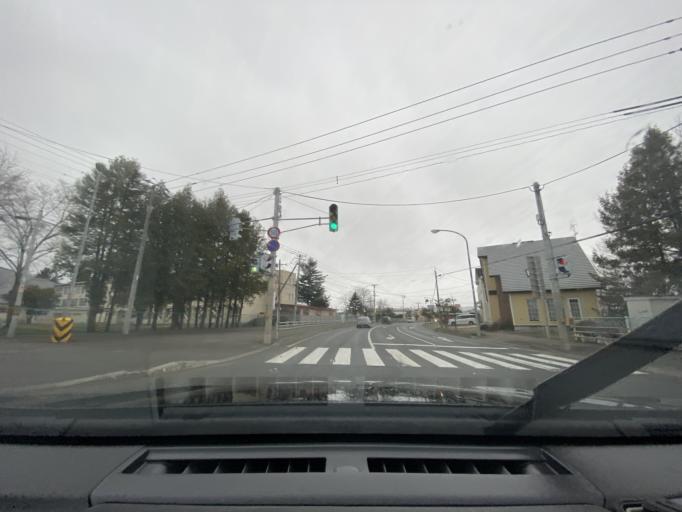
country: JP
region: Hokkaido
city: Kitami
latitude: 43.7996
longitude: 143.9052
